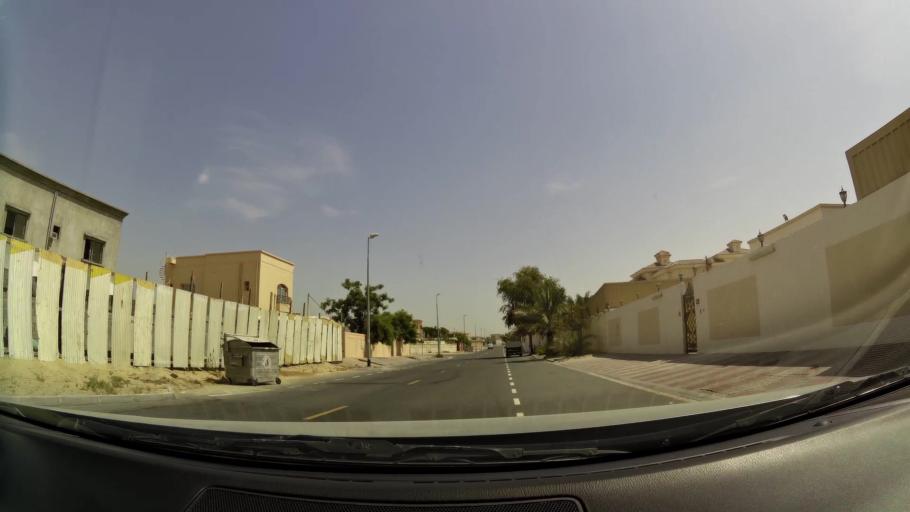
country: AE
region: Ash Shariqah
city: Sharjah
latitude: 25.1852
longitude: 55.4266
